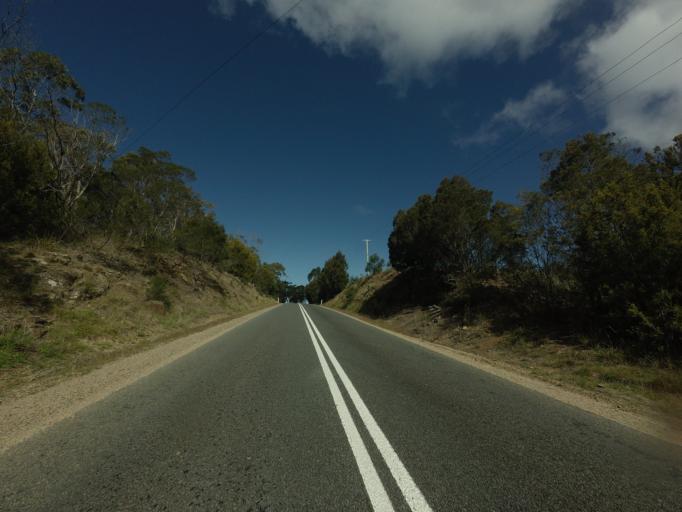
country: AU
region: Tasmania
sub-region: Break O'Day
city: St Helens
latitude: -41.7843
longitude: 148.2589
